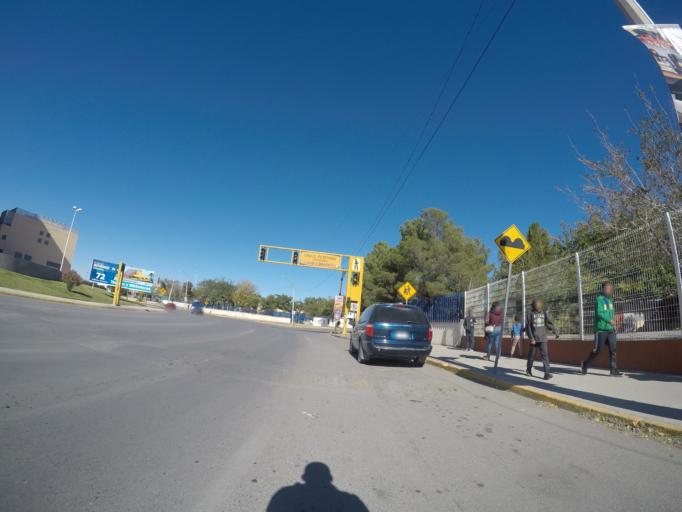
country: MX
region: Chihuahua
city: Ciudad Juarez
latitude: 31.7443
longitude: -106.4441
